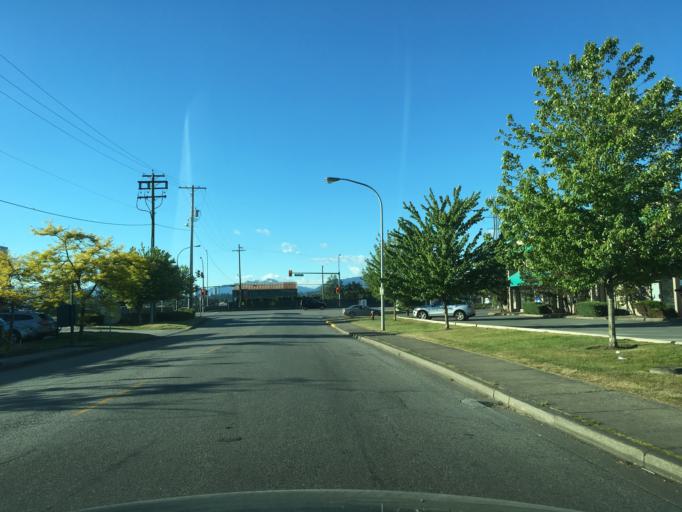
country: CA
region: British Columbia
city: Delta
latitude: 49.1683
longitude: -122.9898
